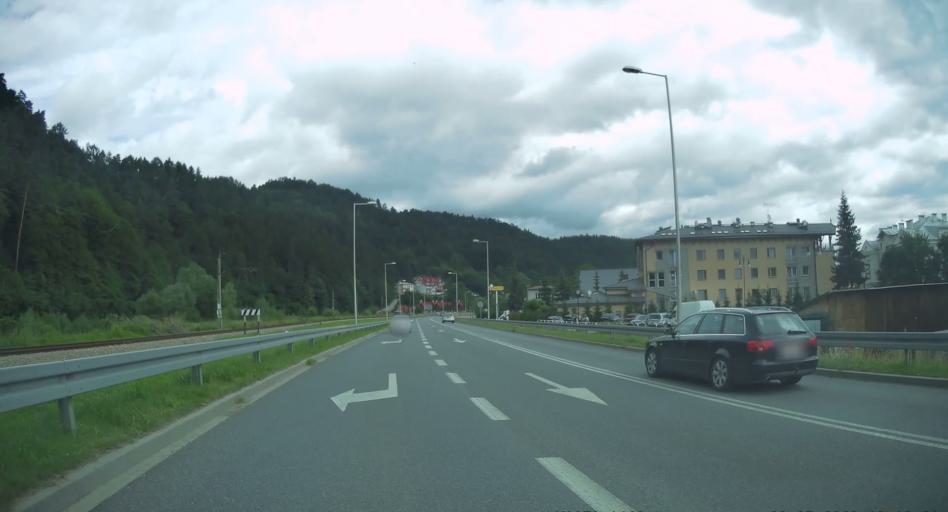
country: PL
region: Lesser Poland Voivodeship
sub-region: Powiat nowosadecki
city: Muszyna
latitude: 49.3550
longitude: 20.8934
